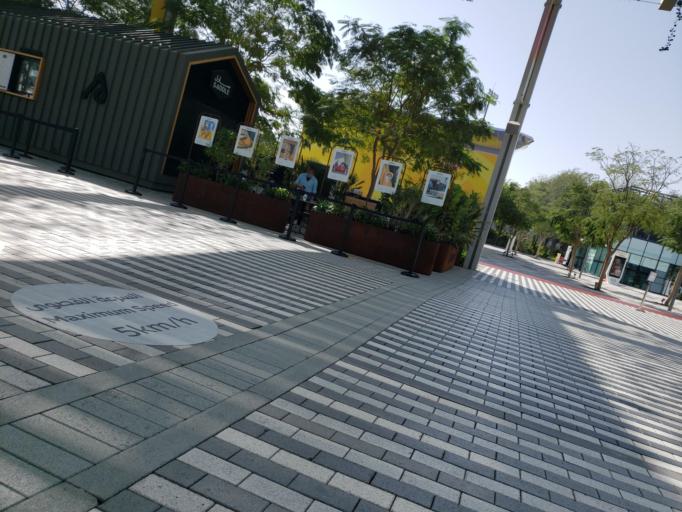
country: AE
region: Dubai
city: Dubai
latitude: 24.9629
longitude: 55.1542
